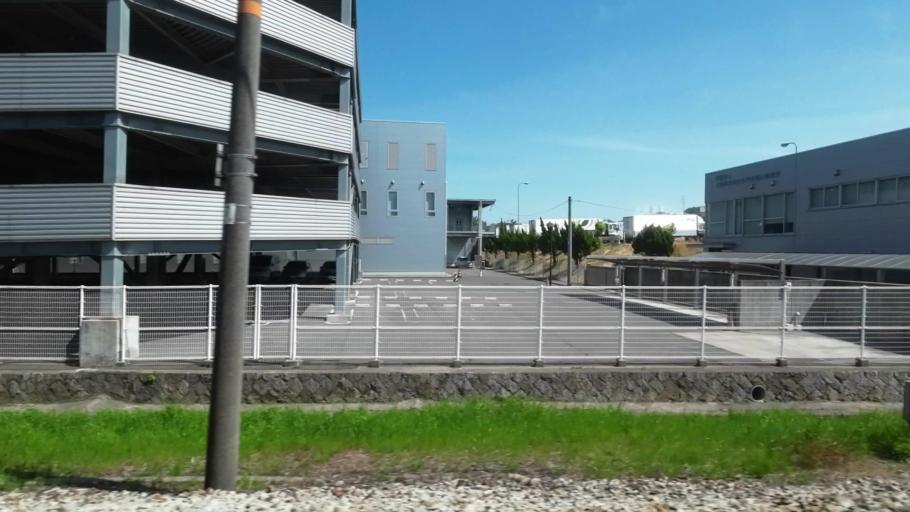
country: JP
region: Hiroshima
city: Fukuyama
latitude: 34.4764
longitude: 133.3132
